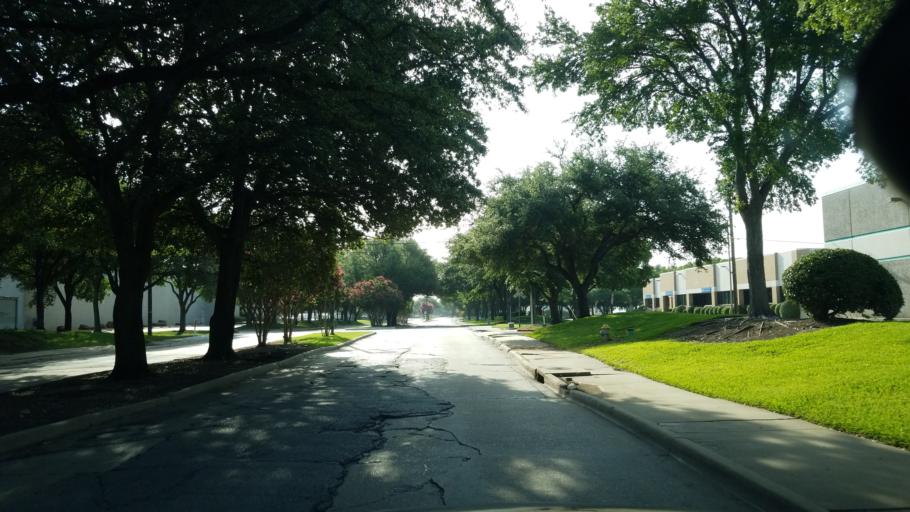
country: US
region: Texas
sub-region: Dallas County
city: Coppell
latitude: 32.9305
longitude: -97.0191
